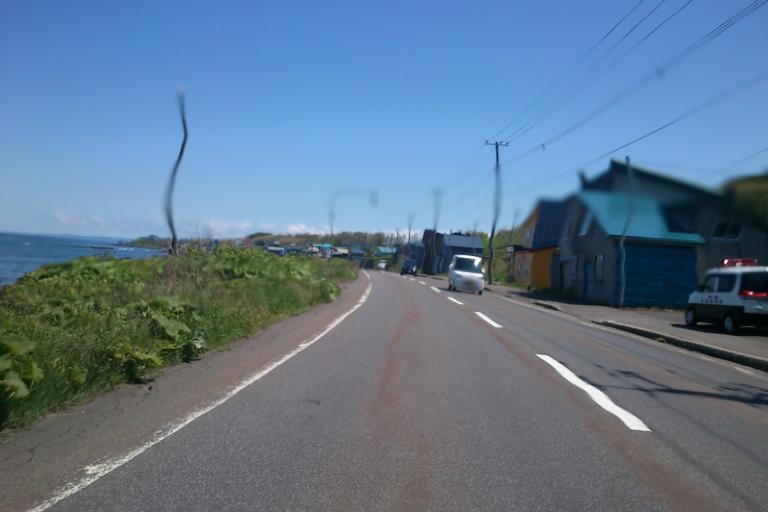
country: JP
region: Hokkaido
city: Rumoi
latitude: 43.8361
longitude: 141.4943
